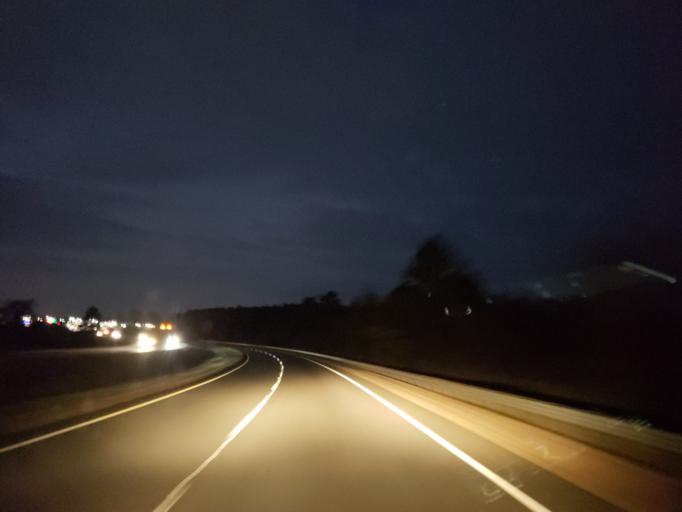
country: US
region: Georgia
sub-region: Polk County
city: Rockmart
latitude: 34.0042
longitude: -85.0258
